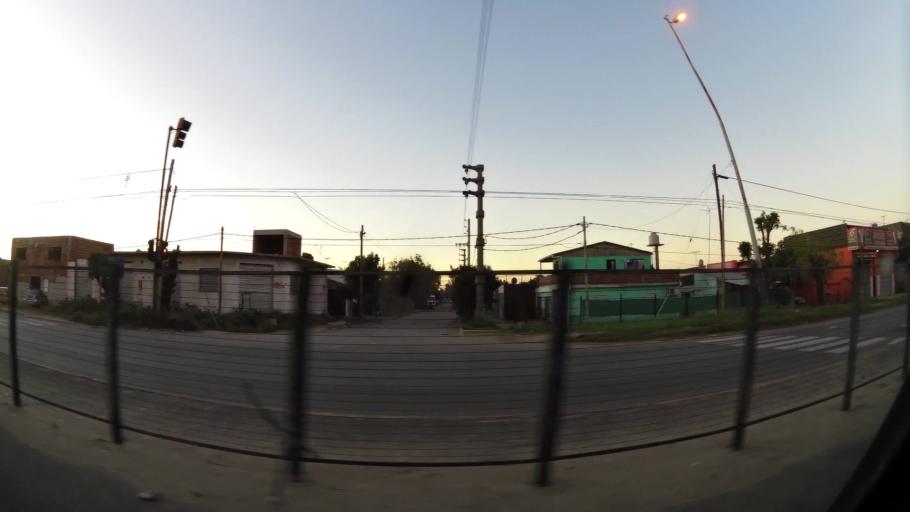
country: AR
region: Buenos Aires
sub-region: Partido de Almirante Brown
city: Adrogue
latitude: -34.7946
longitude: -58.3174
